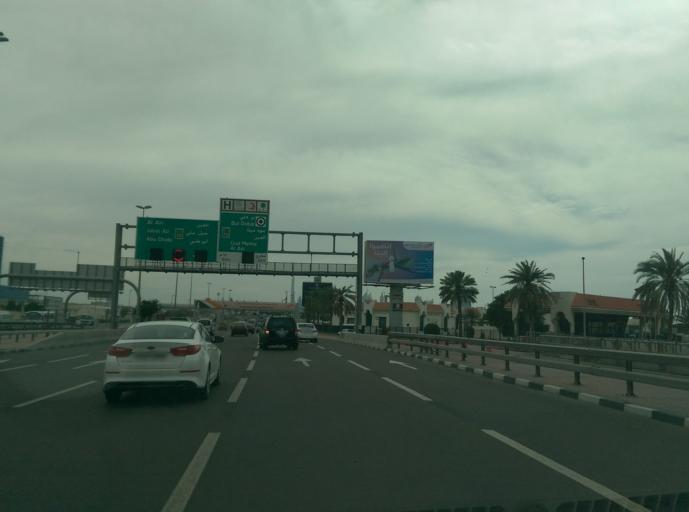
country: AE
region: Ash Shariqah
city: Sharjah
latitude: 25.2556
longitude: 55.3239
